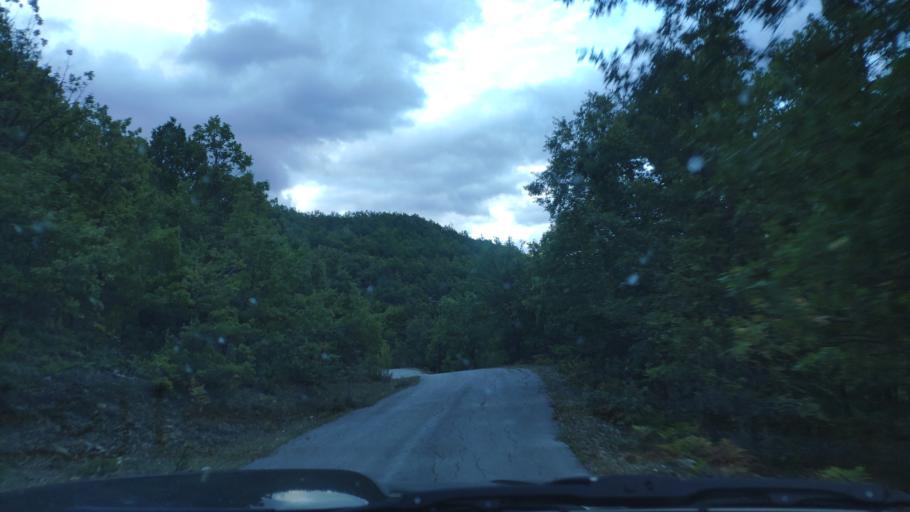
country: AL
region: Korce
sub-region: Rrethi i Kolonjes
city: Erseke
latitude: 40.2547
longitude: 20.8632
